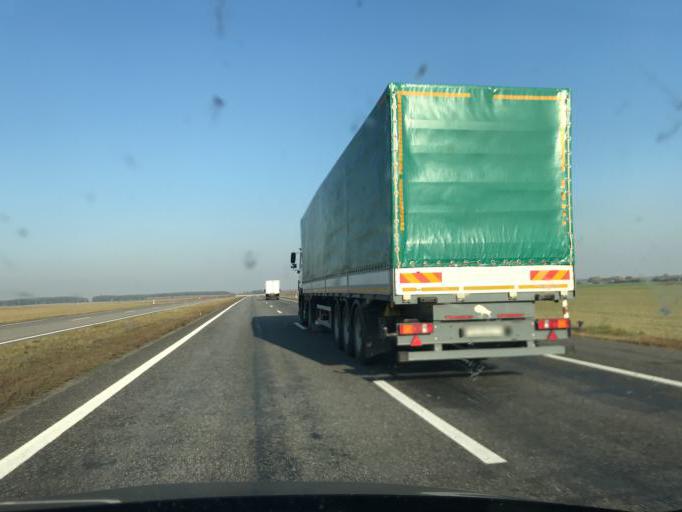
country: BY
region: Minsk
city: Haradzyeya
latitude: 53.3974
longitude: 26.5392
